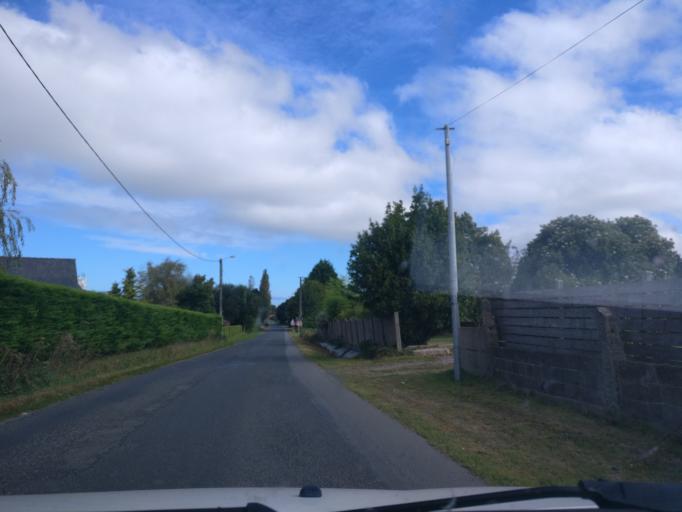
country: FR
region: Brittany
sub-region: Departement des Cotes-d'Armor
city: Rospez
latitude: 48.7609
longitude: -3.3682
